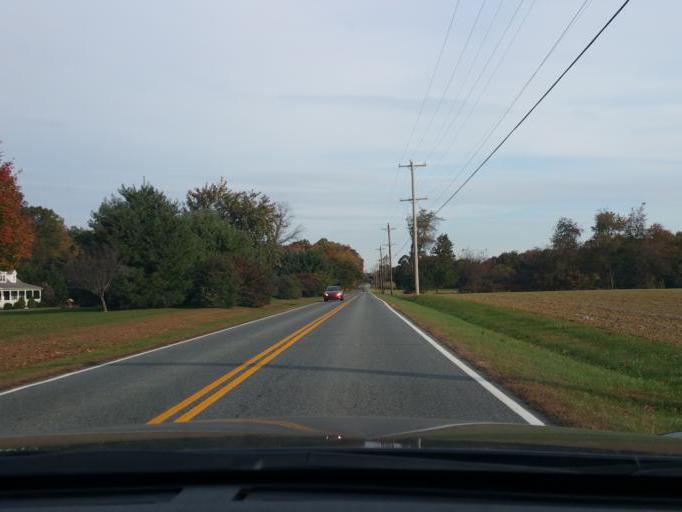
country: US
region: Maryland
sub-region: Cecil County
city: Rising Sun
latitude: 39.7147
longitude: -76.0270
